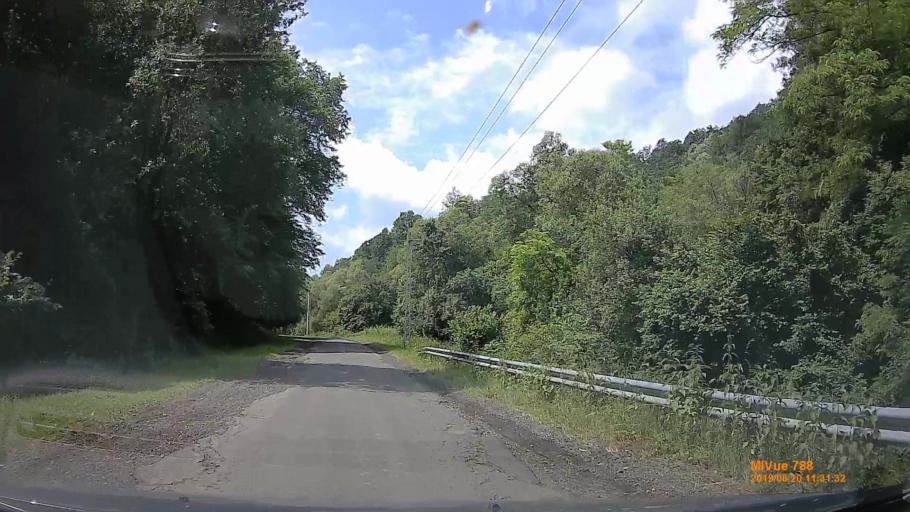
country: HU
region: Baranya
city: Mecseknadasd
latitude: 46.2237
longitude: 18.4298
